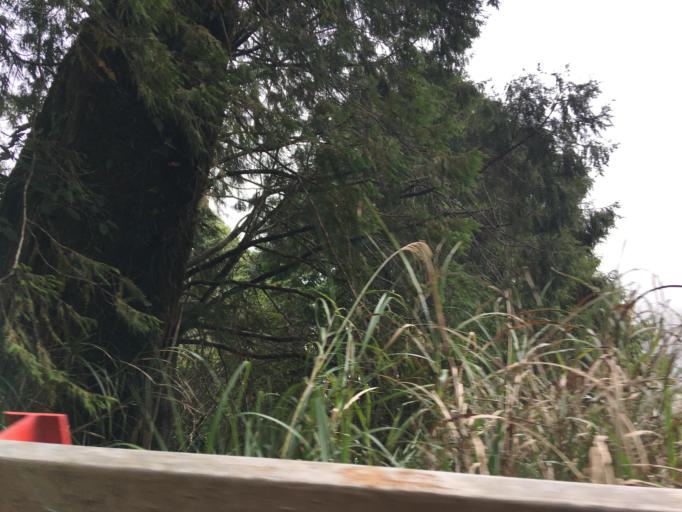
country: TW
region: Taiwan
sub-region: Yilan
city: Yilan
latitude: 24.4839
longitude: 121.5356
